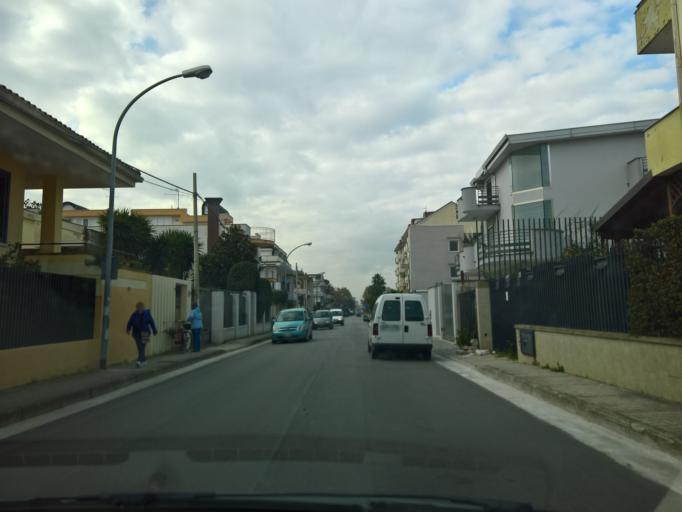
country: IT
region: Campania
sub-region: Provincia di Caserta
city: San Prisco
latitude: 41.0878
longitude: 14.2678
